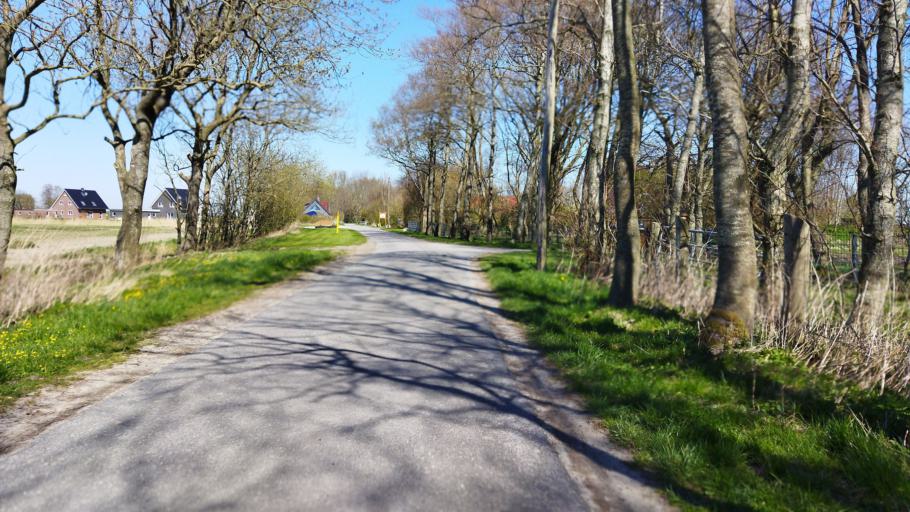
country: DE
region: Lower Saxony
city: Misselwarden
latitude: 53.6929
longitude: 8.4908
